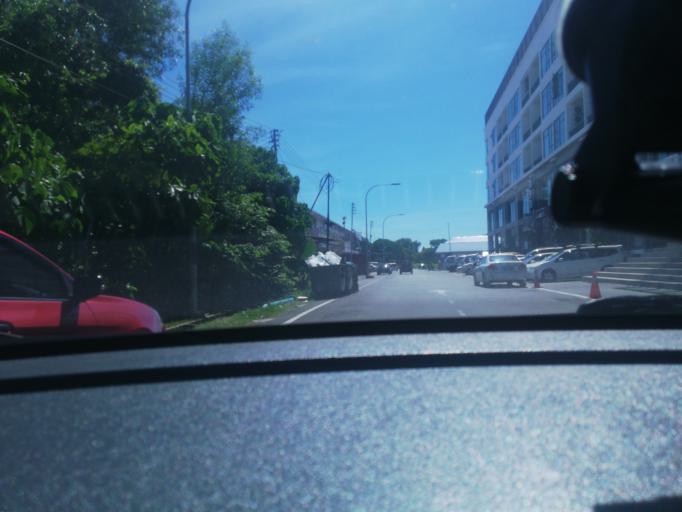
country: MY
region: Labuan
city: Victoria
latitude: 5.2809
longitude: 115.2443
